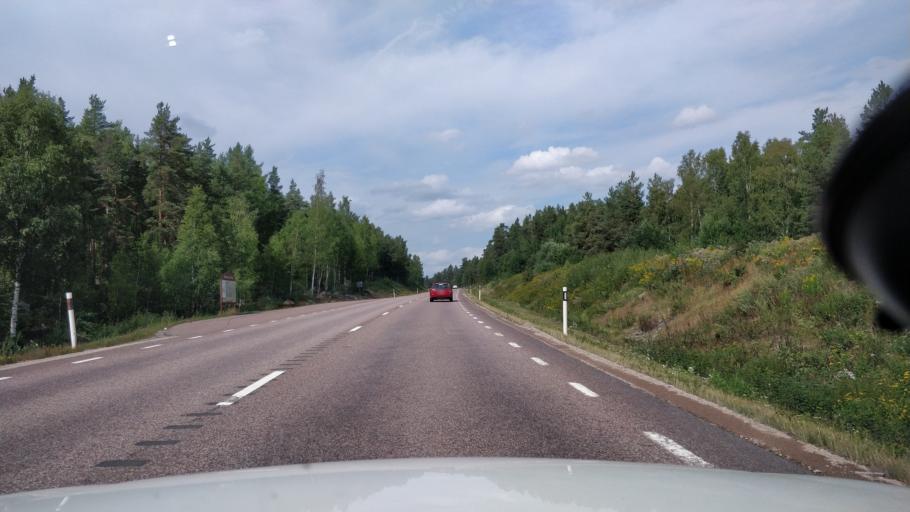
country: SE
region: Dalarna
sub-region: Faluns Kommun
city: Falun
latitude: 60.6322
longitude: 15.5940
